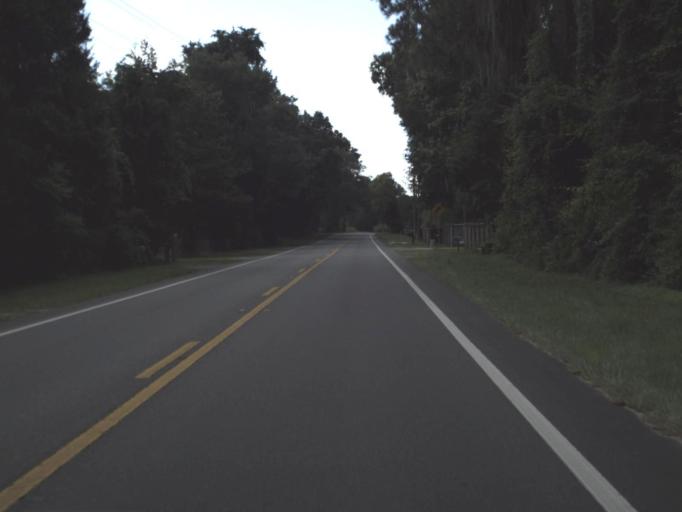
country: US
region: Florida
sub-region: Clay County
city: Keystone Heights
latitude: 29.6976
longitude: -82.0411
